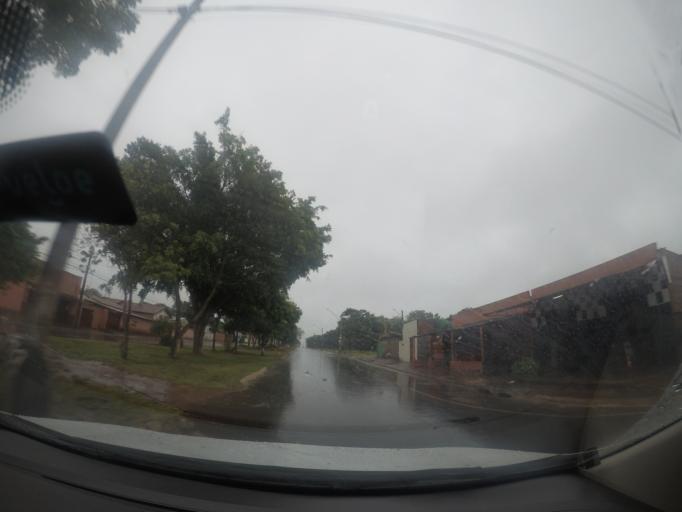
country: BR
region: Goias
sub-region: Goiania
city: Goiania
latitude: -16.6004
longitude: -49.3400
